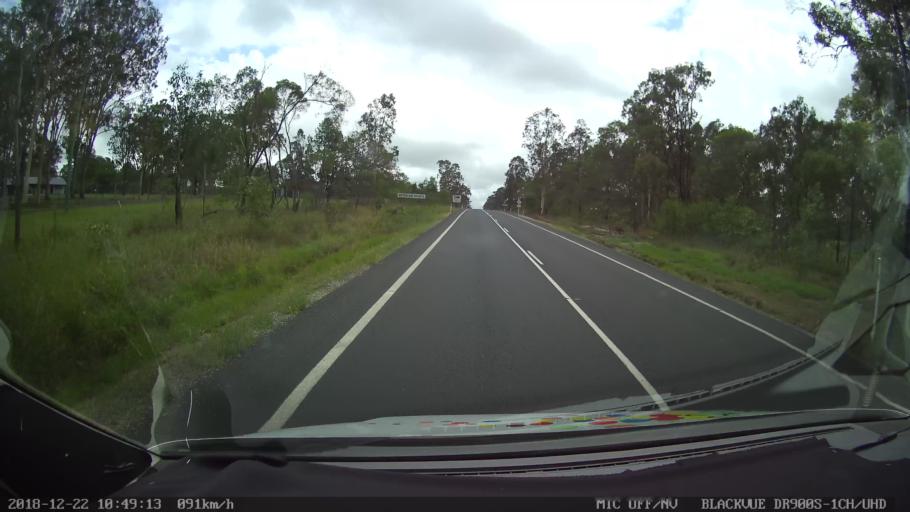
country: AU
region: New South Wales
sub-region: Clarence Valley
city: South Grafton
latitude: -29.6853
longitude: 152.8645
